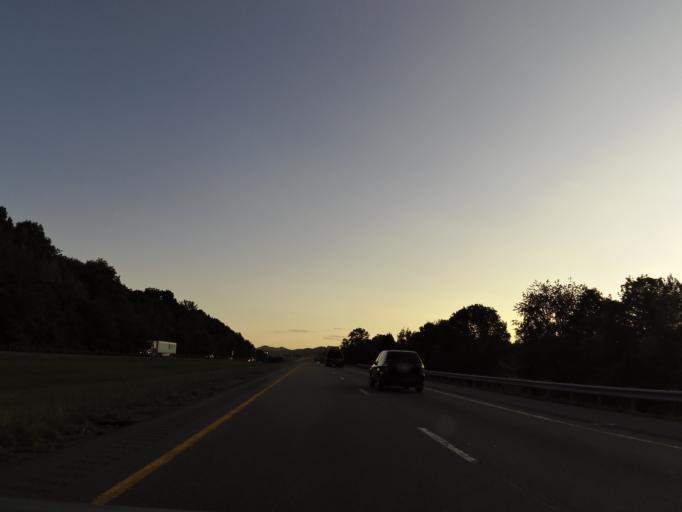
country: US
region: Tennessee
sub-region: Sullivan County
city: Colonial Heights
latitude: 36.4606
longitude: -82.5132
